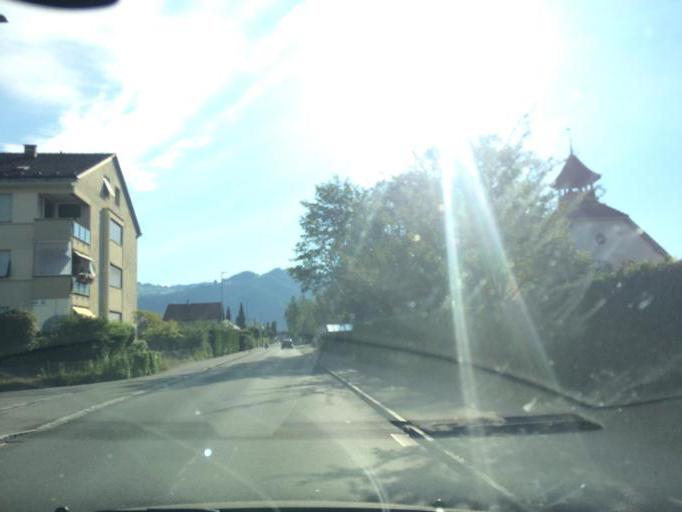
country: CH
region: Bern
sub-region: Thun District
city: Thun
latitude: 46.7391
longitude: 7.6172
